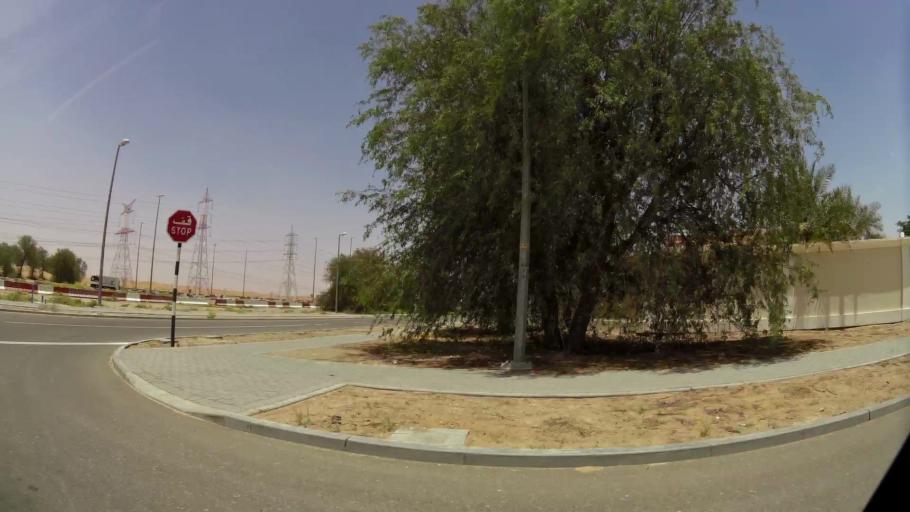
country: OM
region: Al Buraimi
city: Al Buraymi
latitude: 24.2713
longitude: 55.7098
